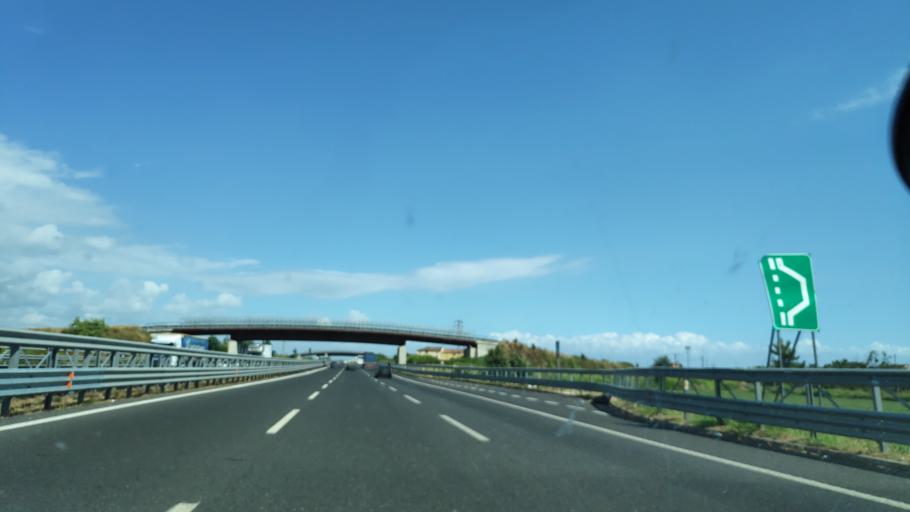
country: IT
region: Campania
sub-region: Provincia di Salerno
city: Pontecagnano
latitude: 40.6507
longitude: 14.8777
